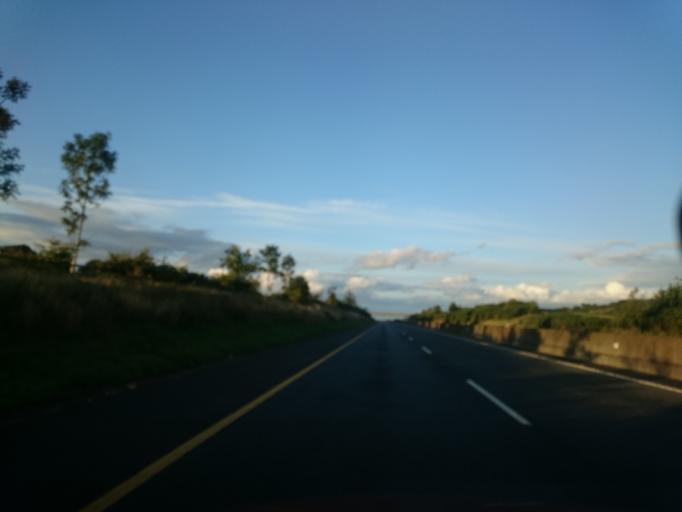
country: IE
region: Leinster
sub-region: Loch Garman
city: Gorey
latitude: 52.6474
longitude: -6.3254
